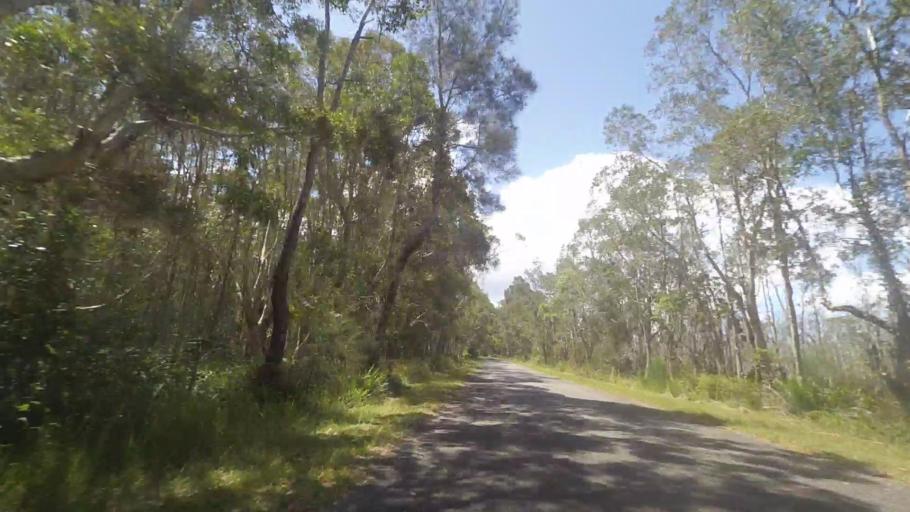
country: AU
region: New South Wales
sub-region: Great Lakes
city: Bulahdelah
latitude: -32.5233
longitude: 152.3229
